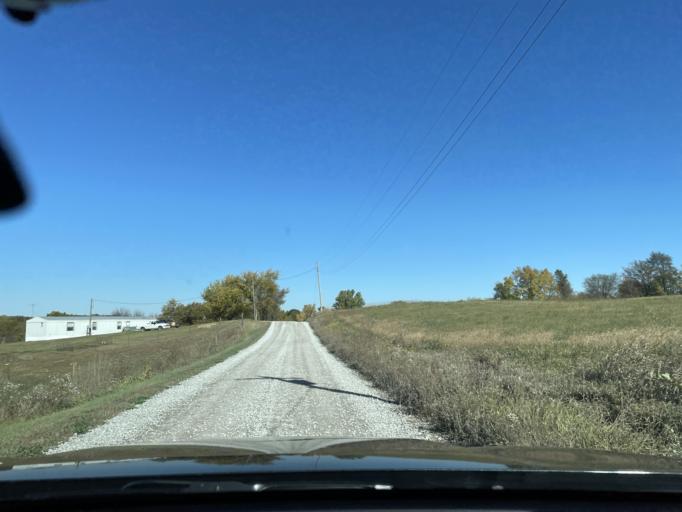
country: US
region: Missouri
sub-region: Andrew County
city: Savannah
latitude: 39.9324
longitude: -94.8805
